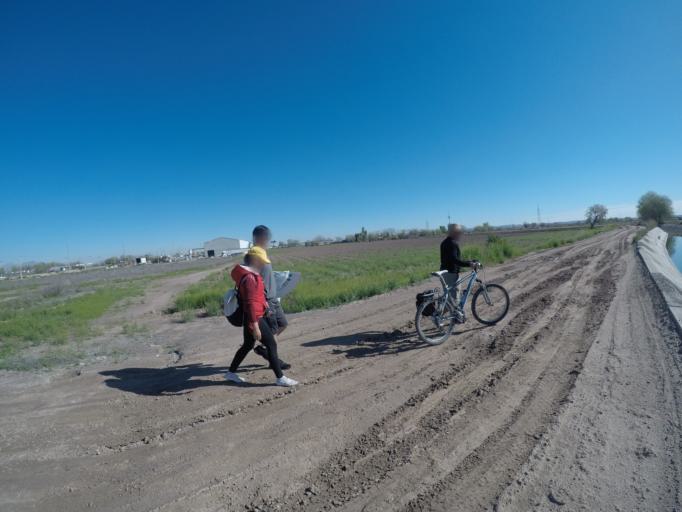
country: US
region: Texas
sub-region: El Paso County
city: Socorro
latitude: 31.6479
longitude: -106.3429
